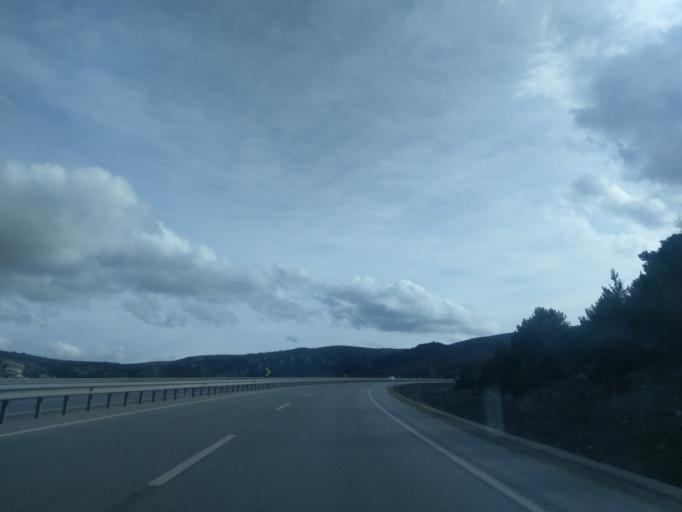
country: TR
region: Kuetahya
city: Sabuncu
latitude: 39.5621
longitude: 30.0760
